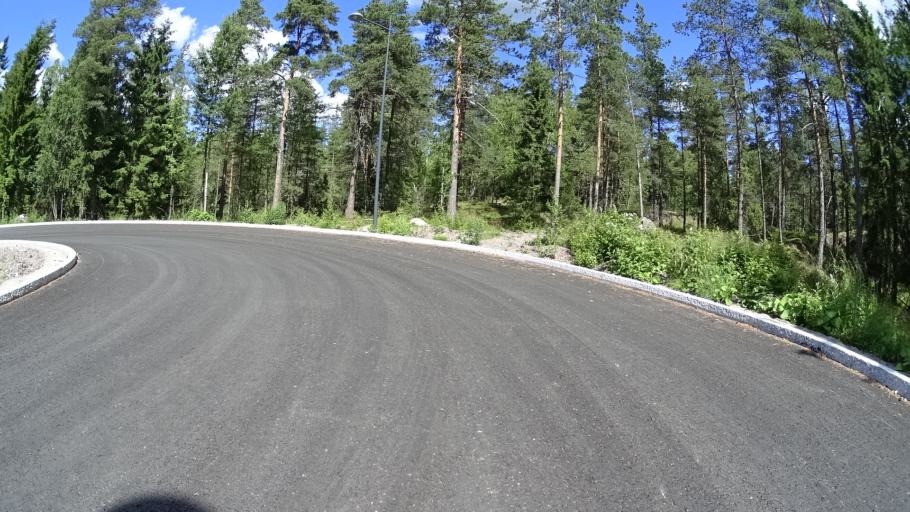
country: FI
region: Uusimaa
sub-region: Helsinki
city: Espoo
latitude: 60.2011
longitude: 24.6093
